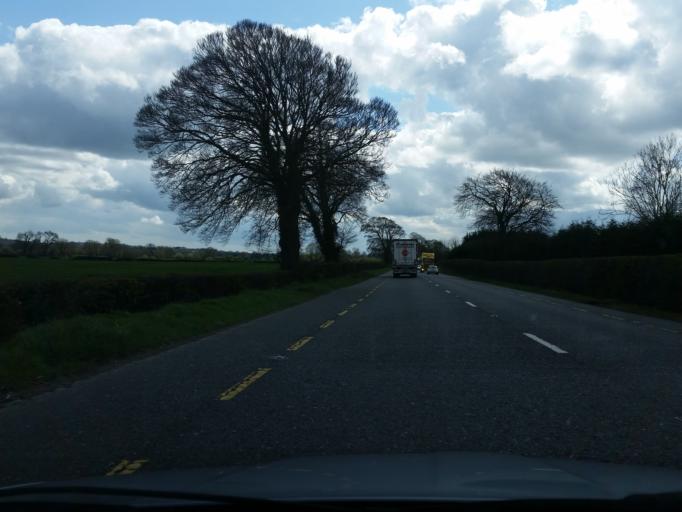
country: IE
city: Kentstown
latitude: 53.6108
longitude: -6.4774
